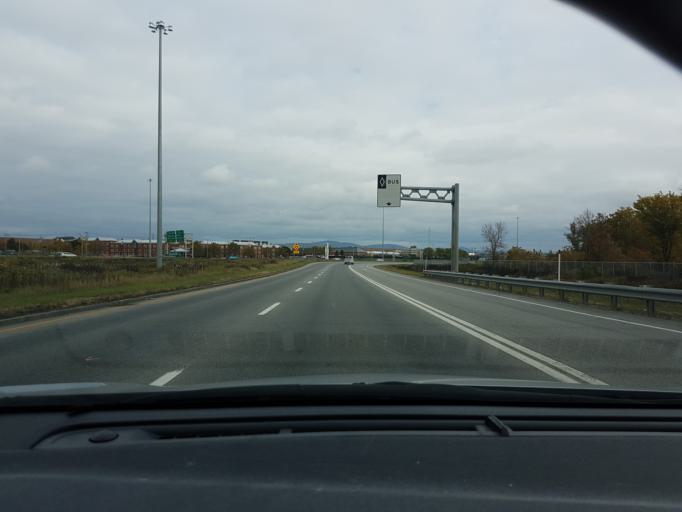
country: CA
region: Quebec
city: L'Ancienne-Lorette
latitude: 46.8237
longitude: -71.2948
